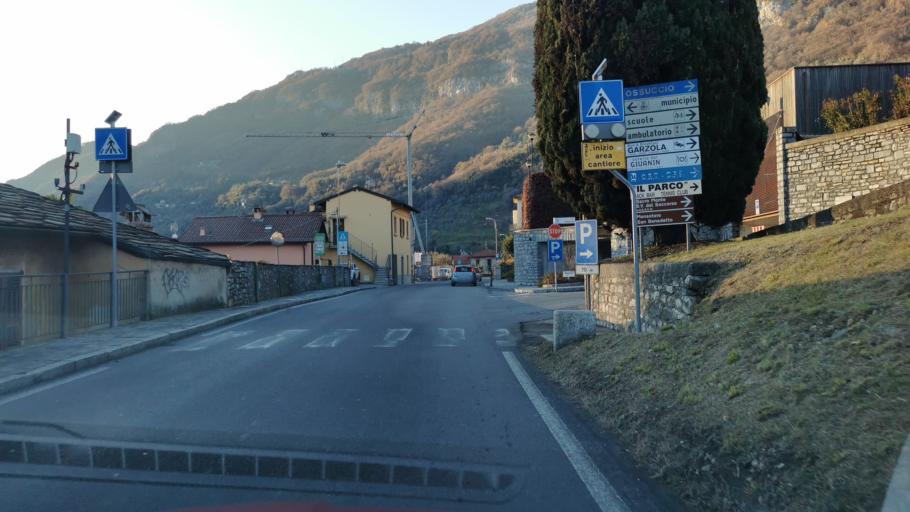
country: IT
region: Lombardy
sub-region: Provincia di Como
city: Ossuccio
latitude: 45.9676
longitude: 9.1808
